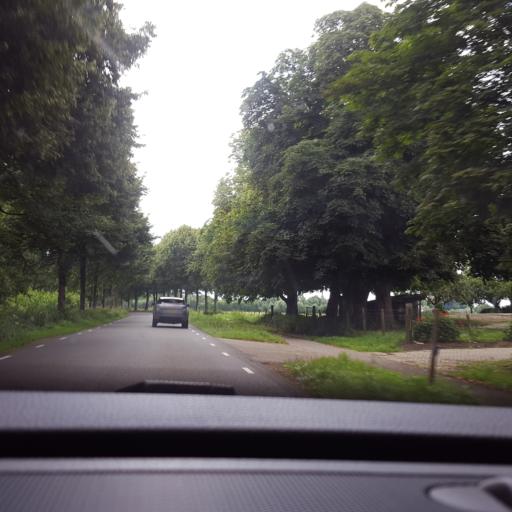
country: NL
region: Gelderland
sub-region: Gemeente Brummen
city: Brummen
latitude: 52.0577
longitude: 6.1754
